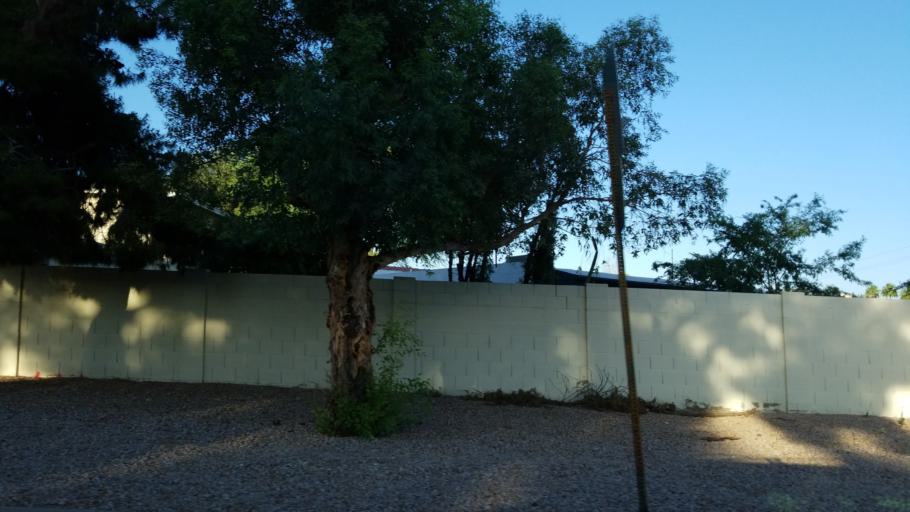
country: US
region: Arizona
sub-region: Maricopa County
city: Scottsdale
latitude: 33.5099
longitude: -111.9174
